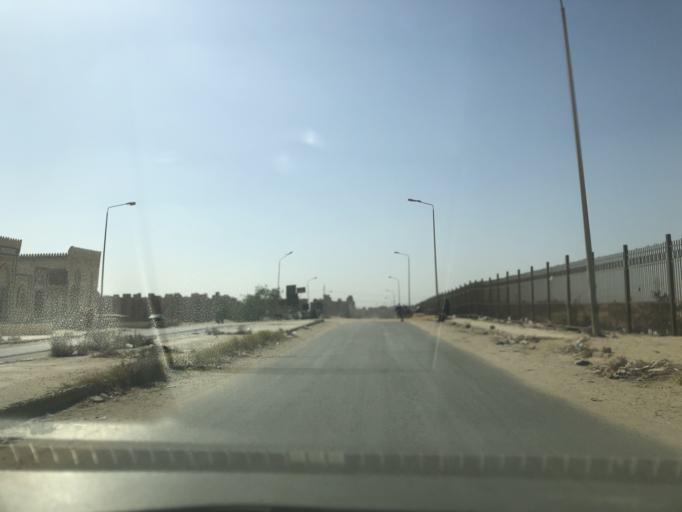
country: EG
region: Al Jizah
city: Madinat Sittah Uktubar
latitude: 29.9274
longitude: 30.9496
